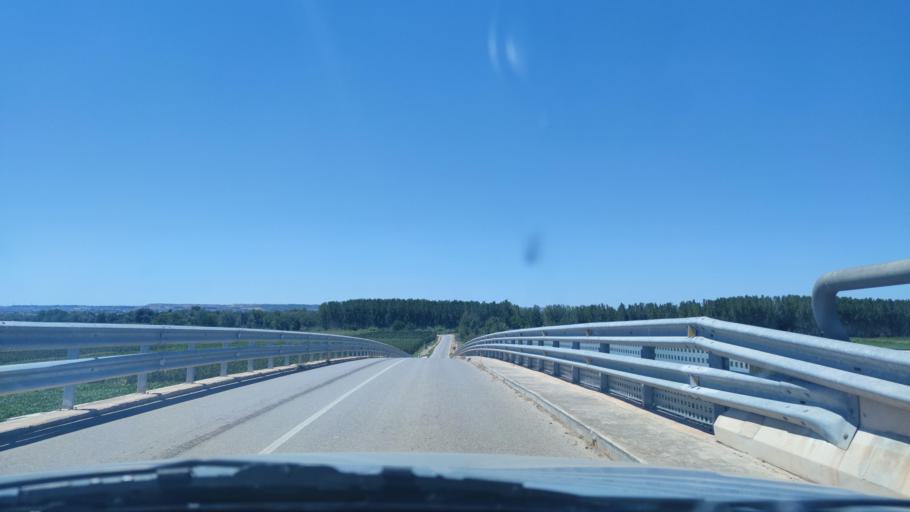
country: ES
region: Catalonia
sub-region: Provincia de Lleida
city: Alcoletge
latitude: 41.6538
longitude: 0.6848
